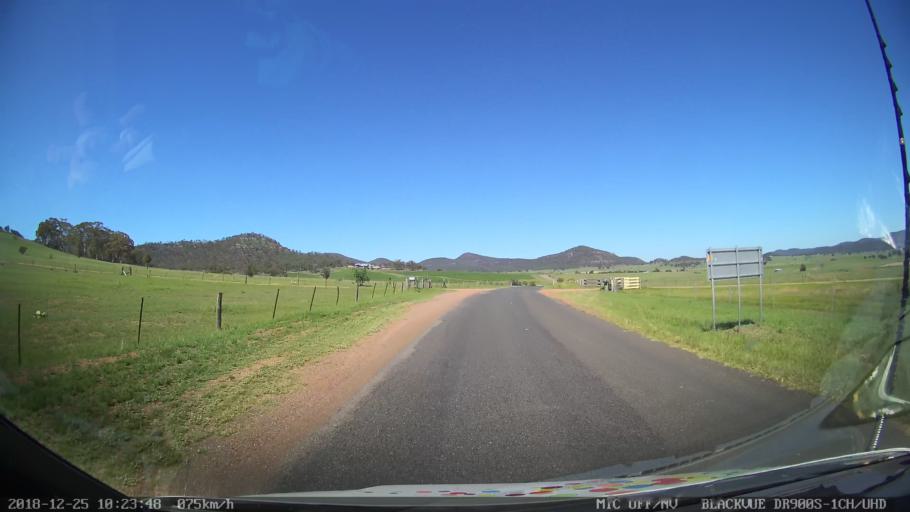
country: AU
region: New South Wales
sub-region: Muswellbrook
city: Denman
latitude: -32.3892
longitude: 150.5205
